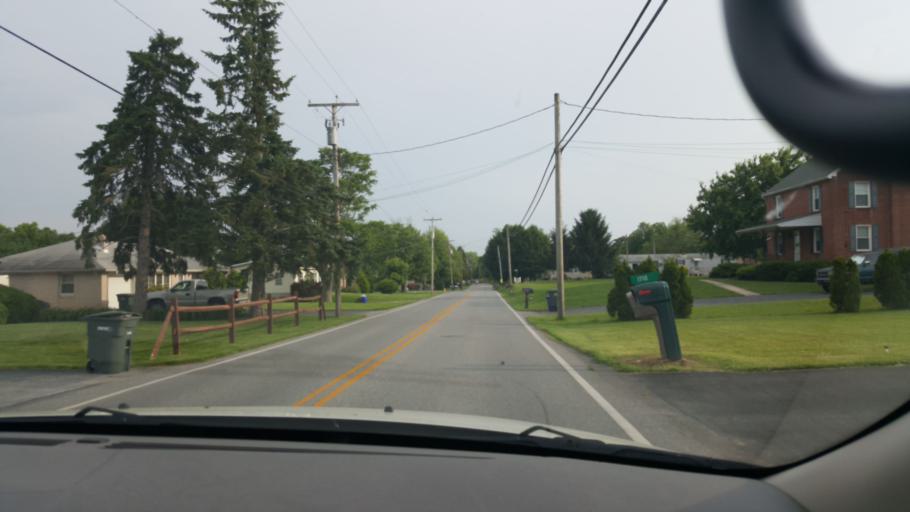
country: US
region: Pennsylvania
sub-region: York County
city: Weigelstown
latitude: 39.9952
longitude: -76.8124
